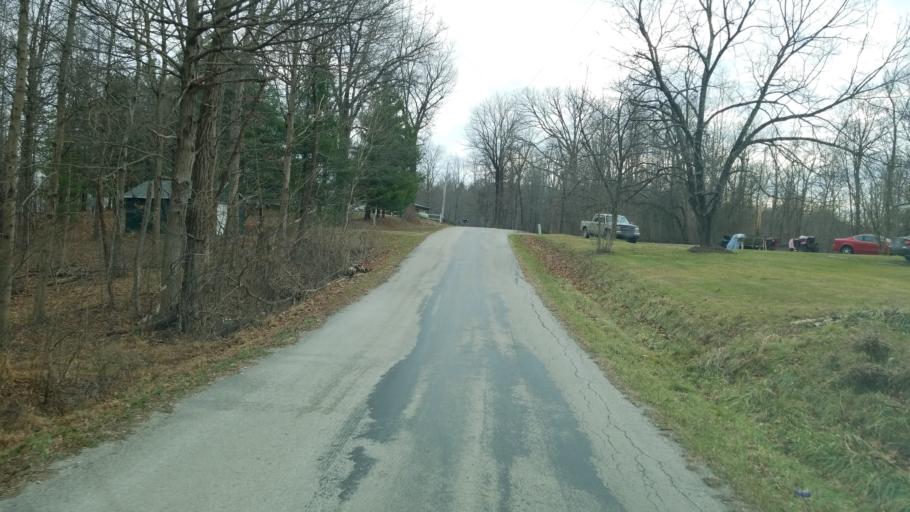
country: US
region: Ohio
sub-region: Highland County
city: Greenfield
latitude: 39.1786
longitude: -83.2687
